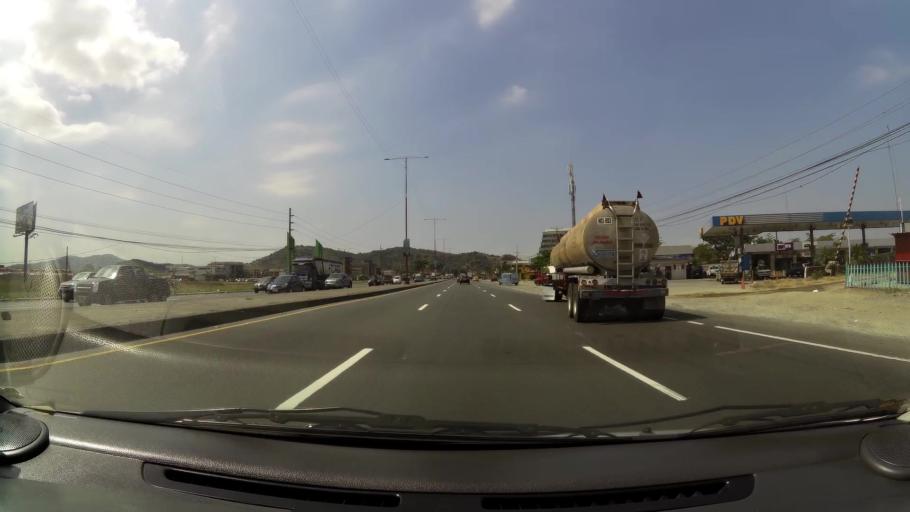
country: EC
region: Guayas
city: El Triunfo
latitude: -2.0522
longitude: -79.9151
